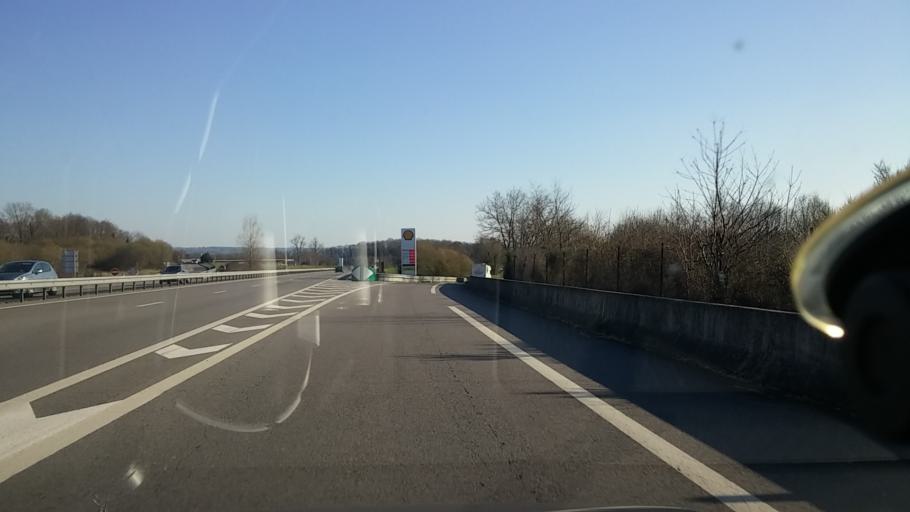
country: FR
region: Limousin
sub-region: Departement de la Haute-Vienne
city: Saint-Sulpice-les-Feuilles
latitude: 46.3174
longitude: 1.4177
